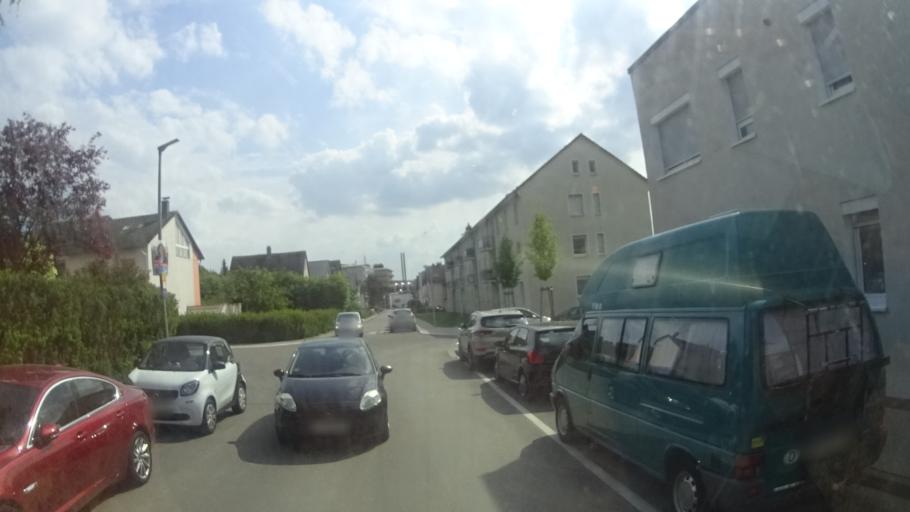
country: DE
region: Baden-Wuerttemberg
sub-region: Karlsruhe Region
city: Bruchsal
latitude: 49.1355
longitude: 8.6053
